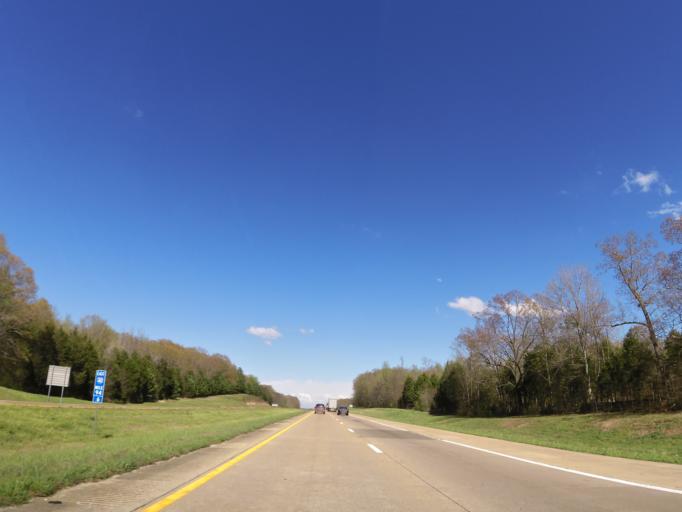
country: US
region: Tennessee
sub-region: Gibson County
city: Medina
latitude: 35.7238
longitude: -88.6153
